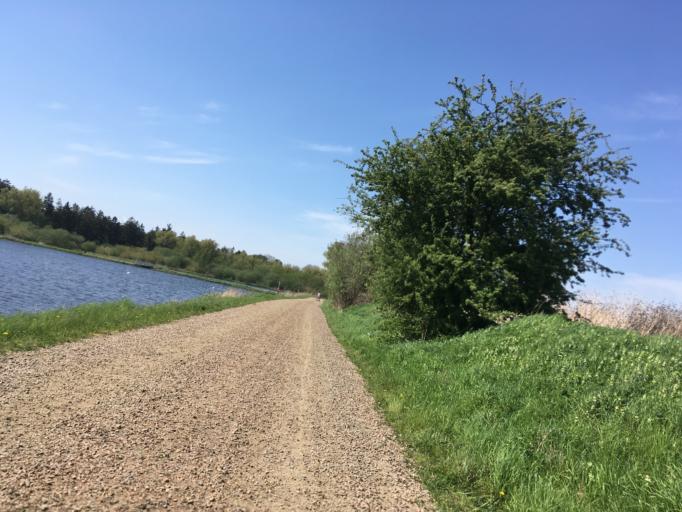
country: SE
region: Skane
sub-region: Staffanstorps Kommun
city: Hjaerup
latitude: 55.6999
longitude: 13.1538
